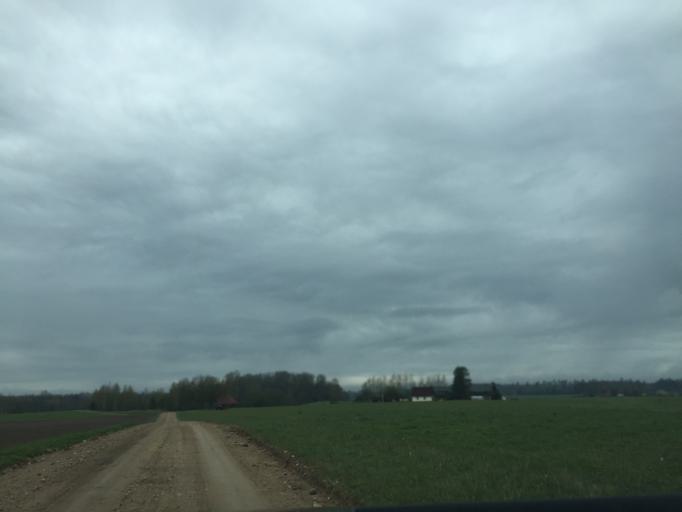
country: LV
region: Sigulda
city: Sigulda
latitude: 57.0359
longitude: 24.8475
